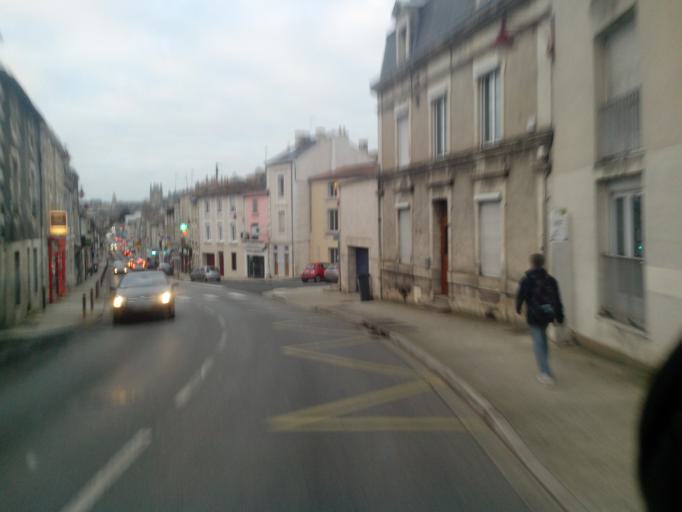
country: FR
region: Poitou-Charentes
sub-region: Departement de la Vienne
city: Poitiers
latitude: 46.5752
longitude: 0.3547
